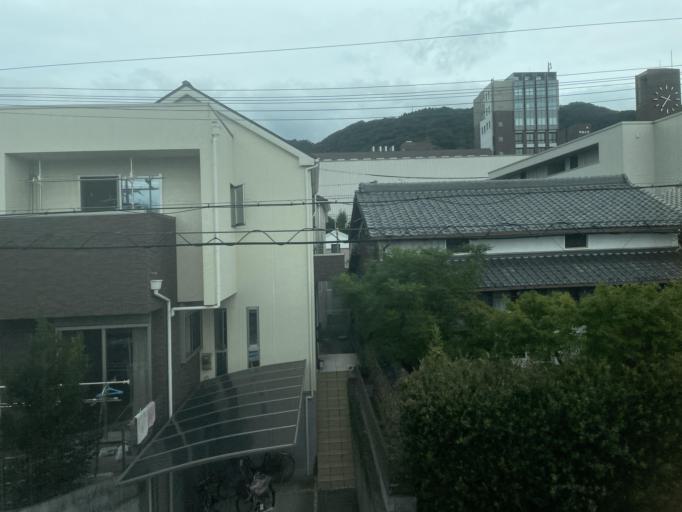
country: JP
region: Hyogo
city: Ashiya
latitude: 34.7274
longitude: 135.2684
